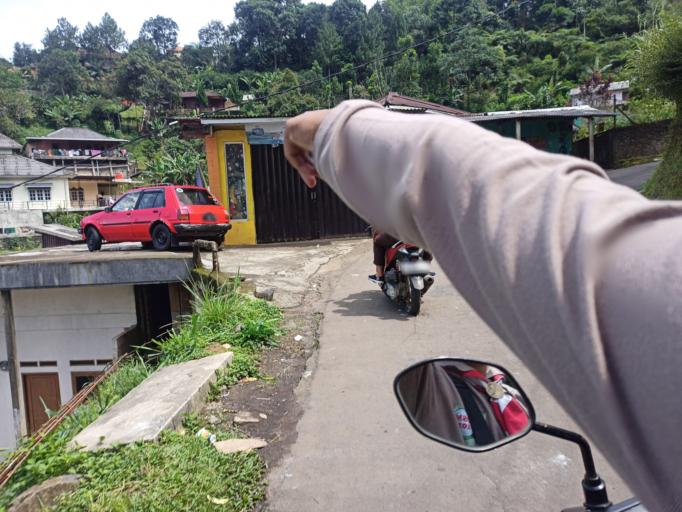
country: ID
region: West Java
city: Caringin
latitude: -6.6427
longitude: 106.9097
